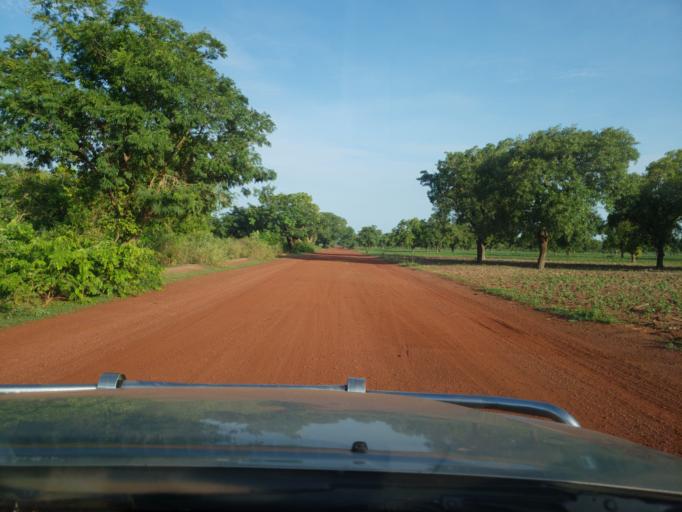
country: ML
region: Sikasso
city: Koutiala
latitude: 12.4135
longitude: -5.5632
